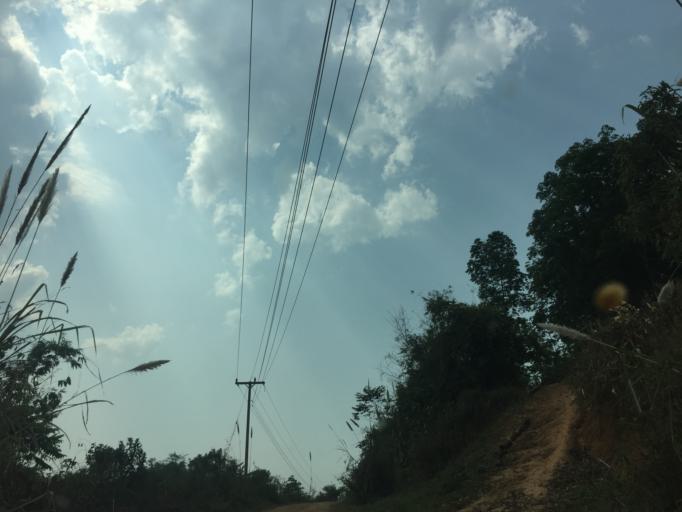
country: TH
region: Nan
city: Song Khwae
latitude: 19.7432
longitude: 100.7064
